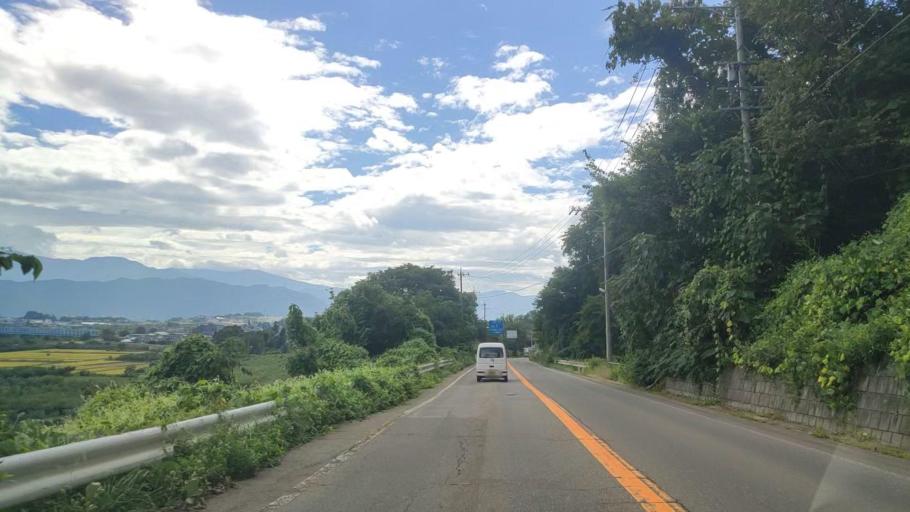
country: JP
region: Nagano
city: Nakano
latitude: 36.7589
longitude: 138.3176
